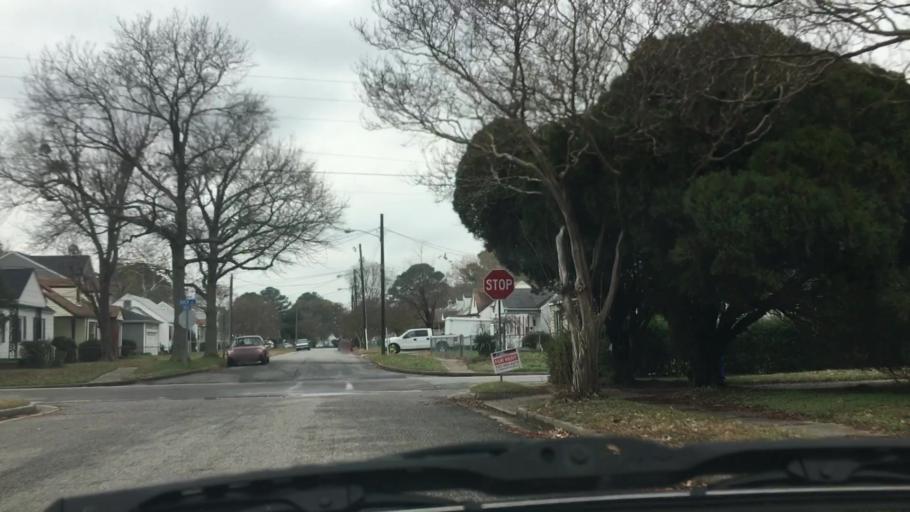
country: US
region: Virginia
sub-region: City of Norfolk
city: Norfolk
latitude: 36.8747
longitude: -76.2387
